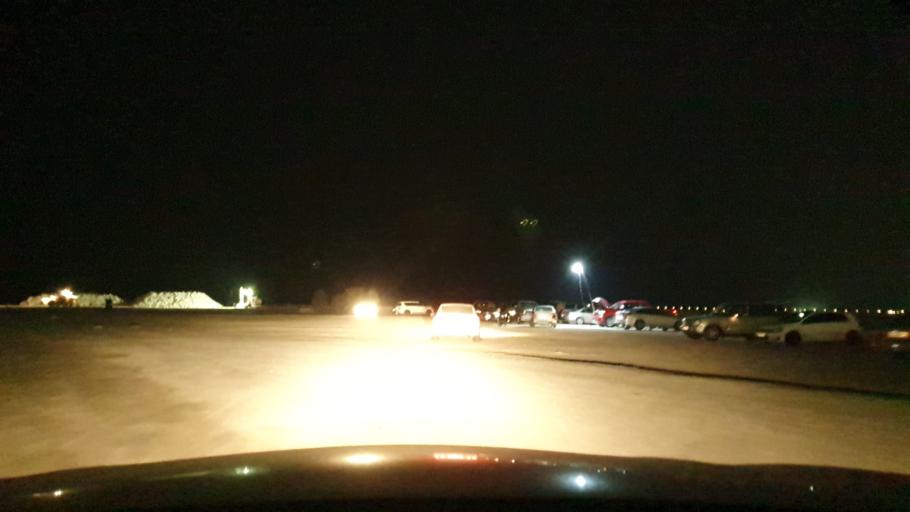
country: BH
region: Muharraq
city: Al Muharraq
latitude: 26.2557
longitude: 50.5839
